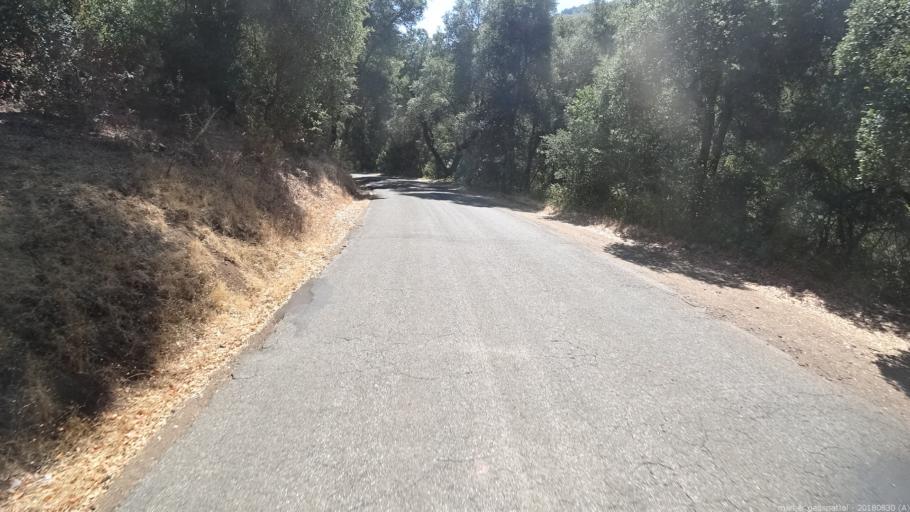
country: US
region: California
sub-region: Monterey County
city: King City
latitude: 36.0126
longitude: -121.4105
